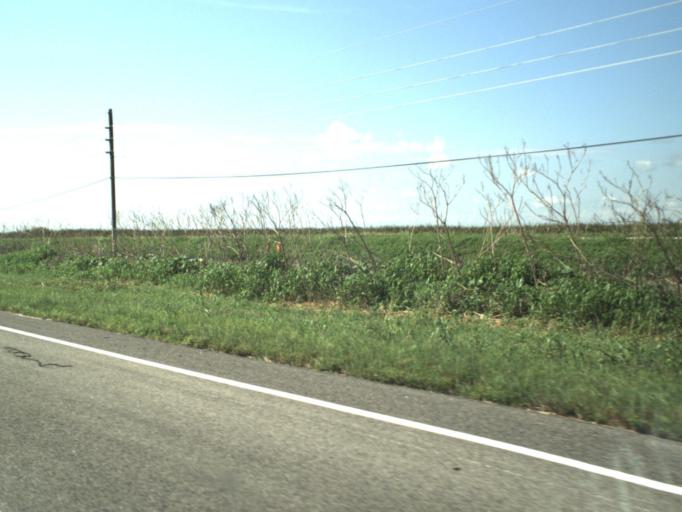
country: US
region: Florida
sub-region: Palm Beach County
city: Belle Glade Camp
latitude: 26.3944
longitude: -80.5840
